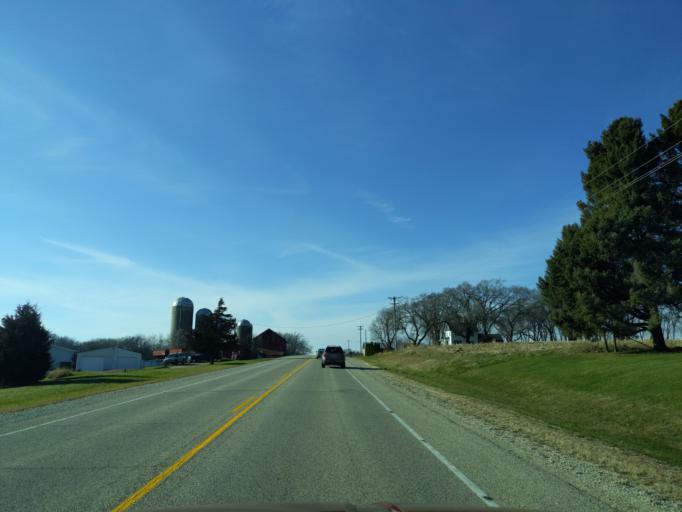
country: US
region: Wisconsin
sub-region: Jefferson County
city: Fort Atkinson
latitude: 42.8291
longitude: -88.8419
